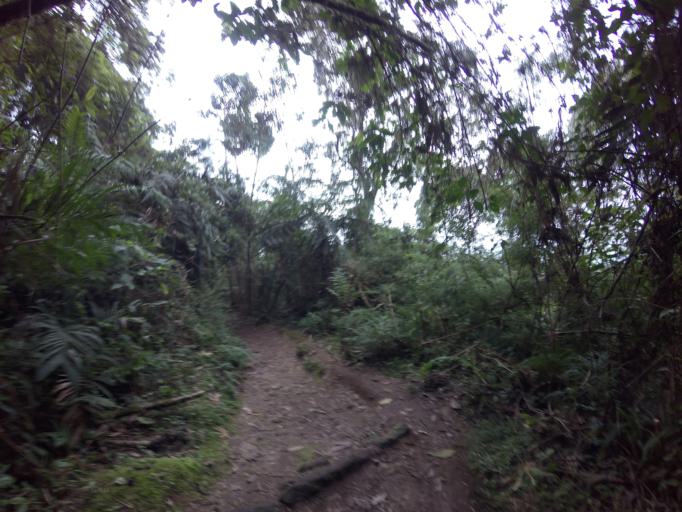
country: CO
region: Cundinamarca
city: San Antonio del Tequendama
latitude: 4.6088
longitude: -74.3073
